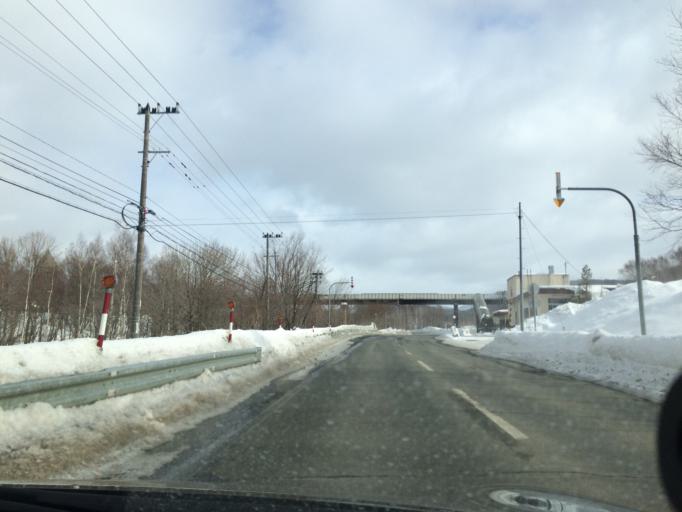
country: JP
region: Hokkaido
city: Shimo-furano
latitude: 43.0565
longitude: 142.6101
